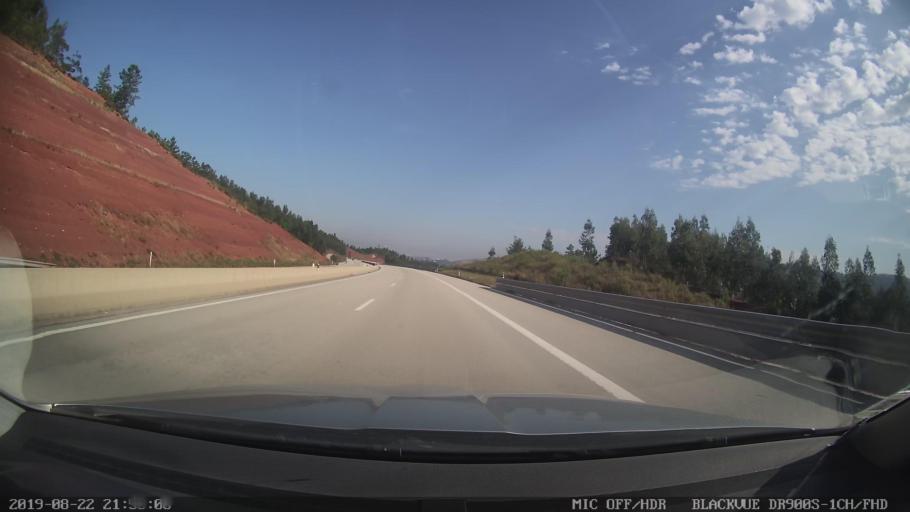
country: PT
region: Coimbra
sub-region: Coimbra
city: Coimbra
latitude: 40.1480
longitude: -8.3832
